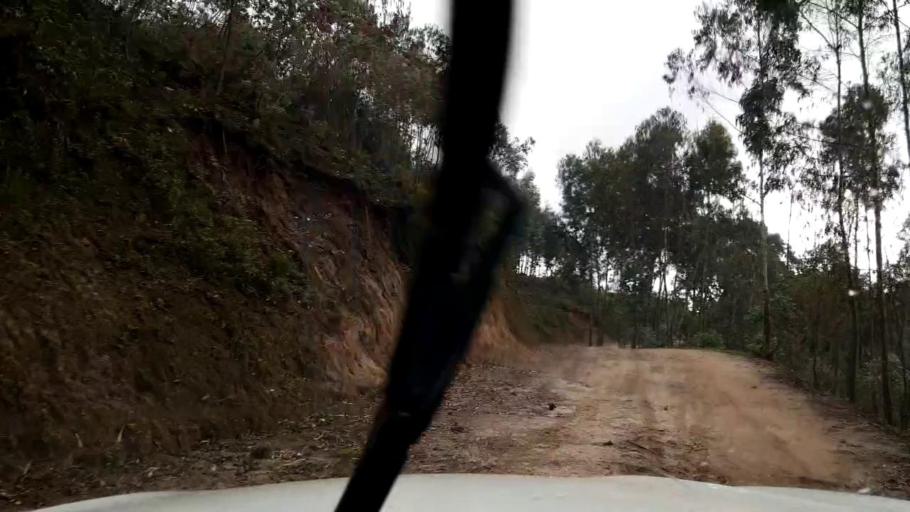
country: RW
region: Western Province
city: Kibuye
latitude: -1.9702
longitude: 29.4866
